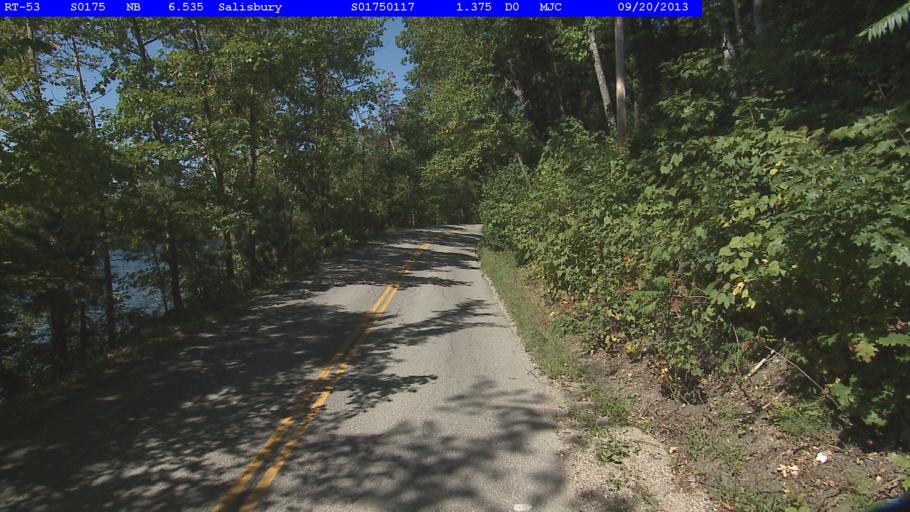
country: US
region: Vermont
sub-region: Rutland County
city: Brandon
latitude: 43.9170
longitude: -73.0689
